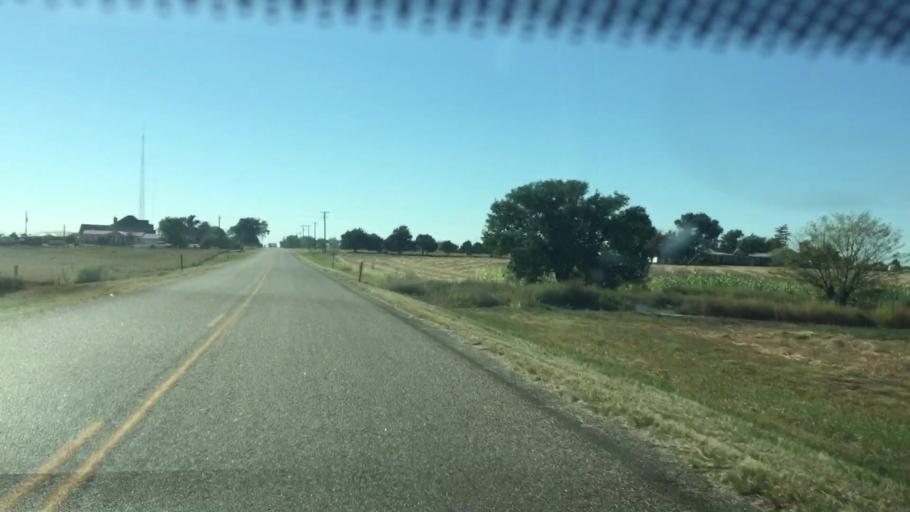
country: US
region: Colorado
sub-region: Prowers County
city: Lamar
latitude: 38.1175
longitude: -102.6107
